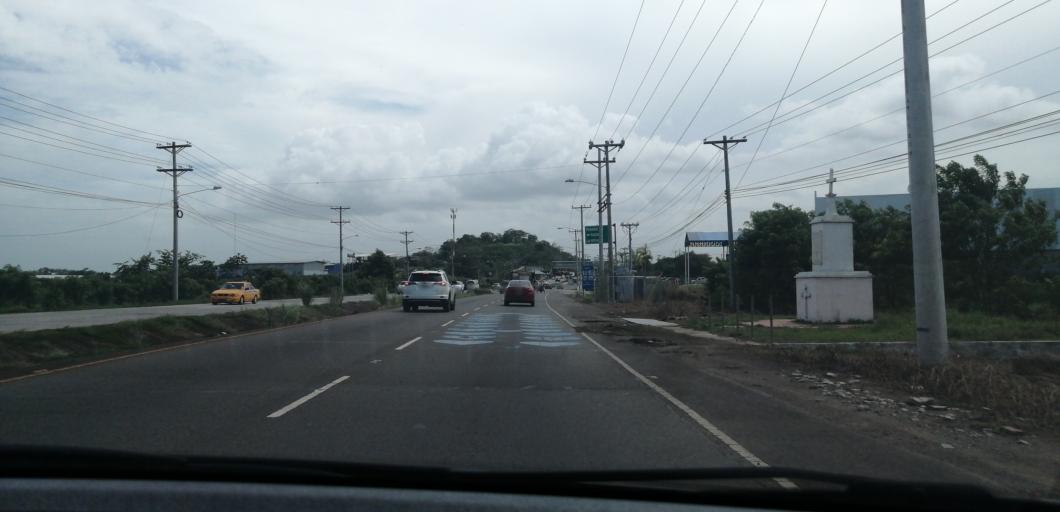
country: PA
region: Panama
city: Pacora
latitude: 9.0992
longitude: -79.2837
